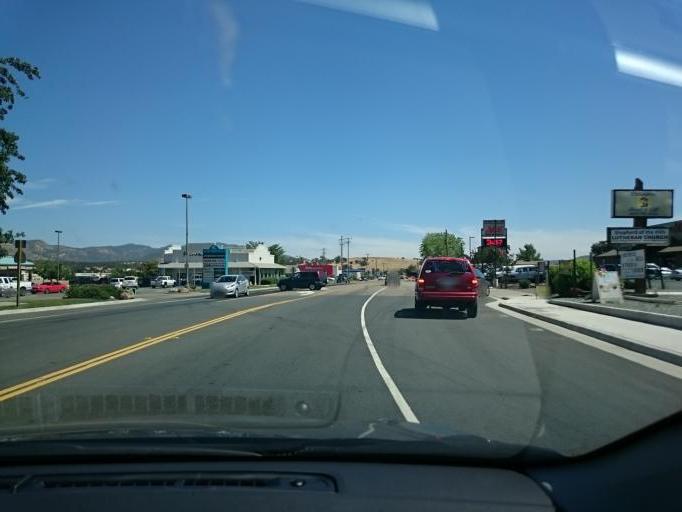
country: US
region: California
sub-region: Calaveras County
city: Valley Springs
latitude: 38.1910
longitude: -120.8283
